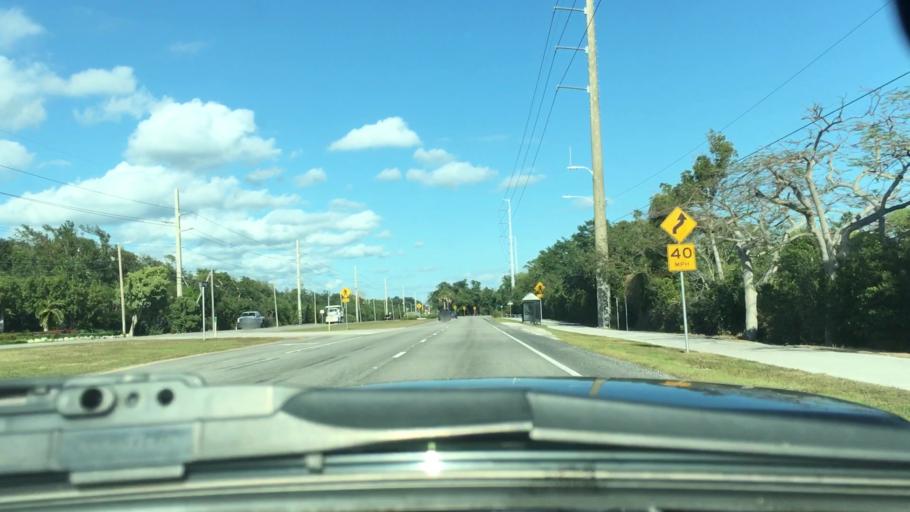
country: US
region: Florida
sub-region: Monroe County
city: Key Largo
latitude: 25.0606
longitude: -80.4759
